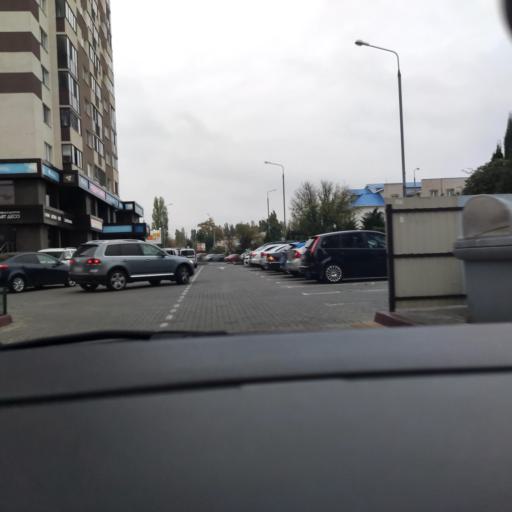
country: RU
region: Voronezj
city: Voronezh
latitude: 51.6546
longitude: 39.1801
